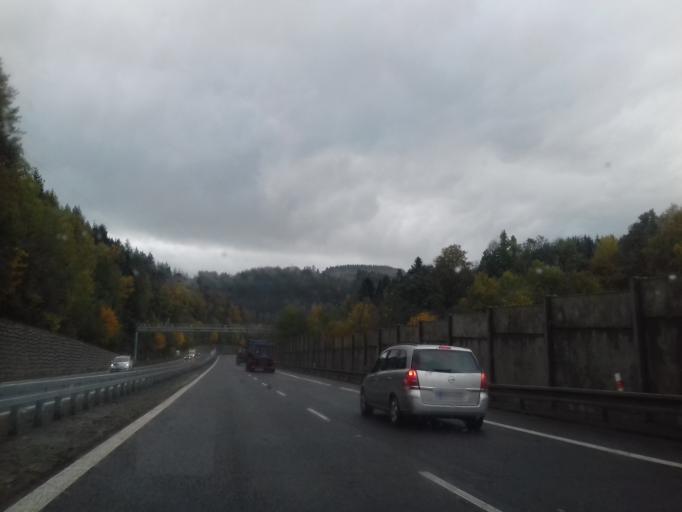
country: CZ
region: Liberecky
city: Hodkovice nad Mohelkou
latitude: 50.6939
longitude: 15.1047
